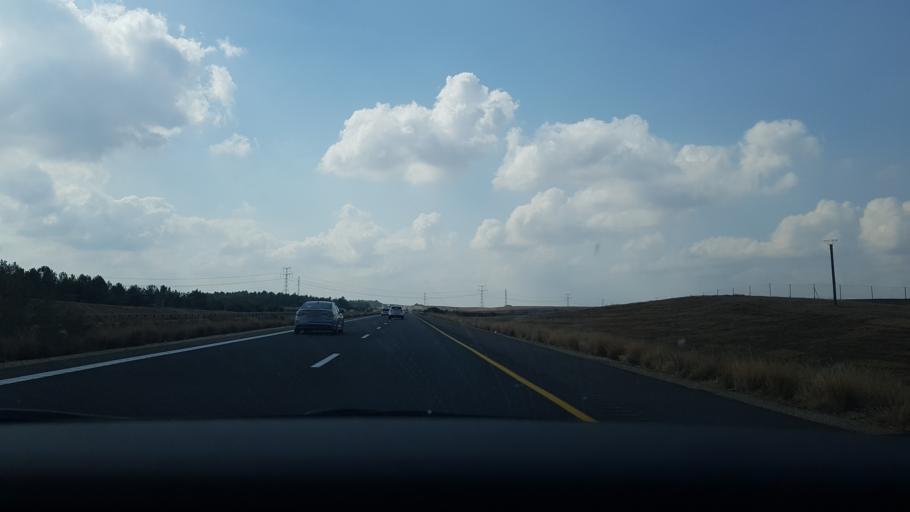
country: IL
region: Southern District
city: Qiryat Gat
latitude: 31.6984
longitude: 34.8158
